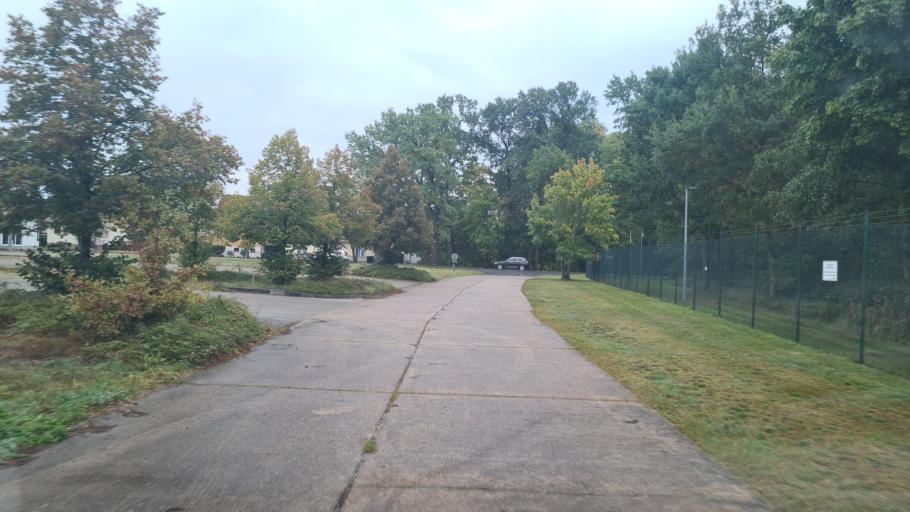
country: DE
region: Brandenburg
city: Storkow
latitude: 52.2422
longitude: 13.9394
